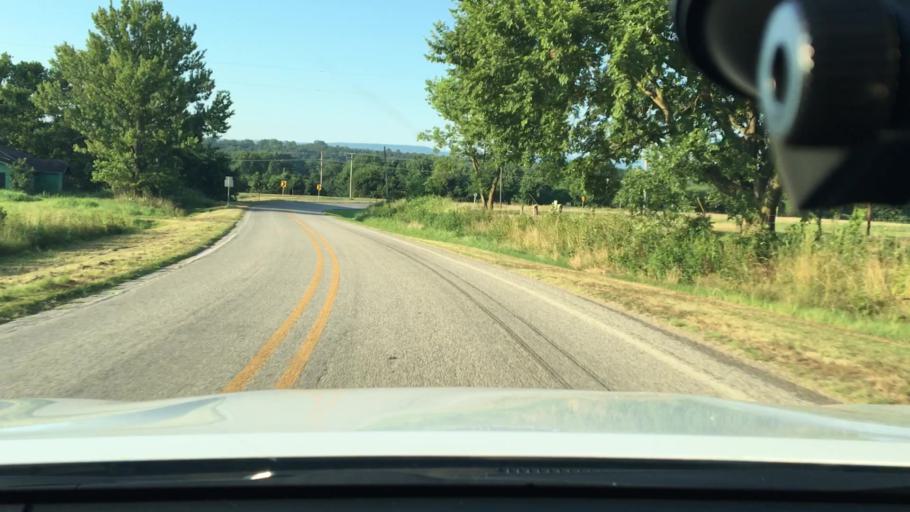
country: US
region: Arkansas
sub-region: Johnson County
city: Coal Hill
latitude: 35.3388
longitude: -93.6038
